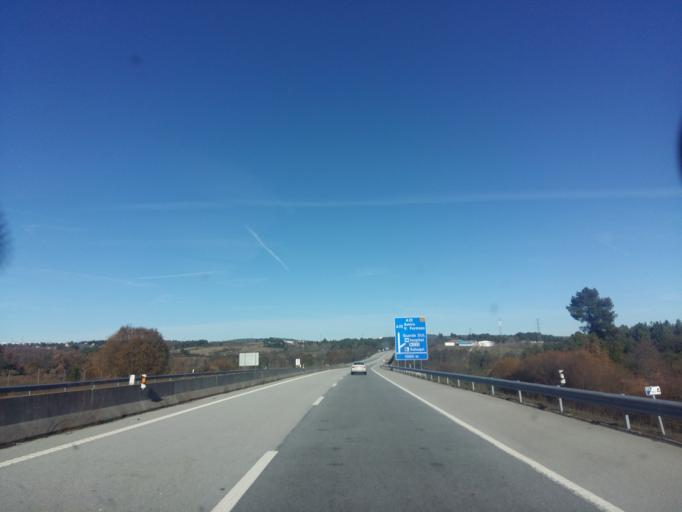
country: PT
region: Guarda
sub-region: Guarda
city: Guarda
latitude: 40.5113
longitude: -7.2344
